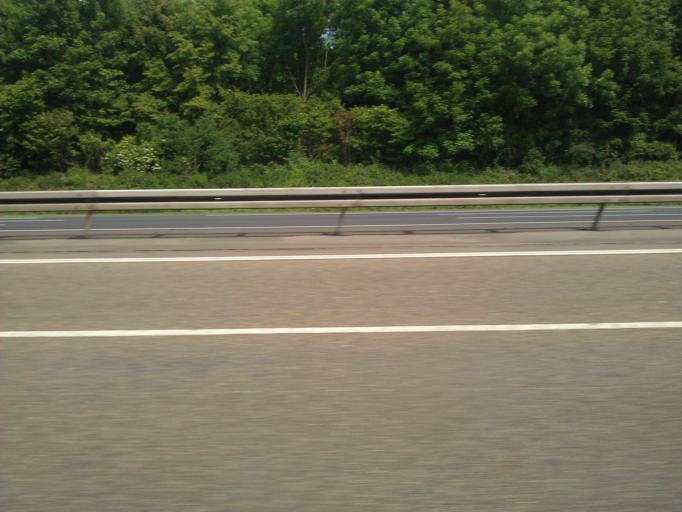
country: DE
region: North Rhine-Westphalia
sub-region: Regierungsbezirk Koln
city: Neustadt/Sued
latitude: 50.8977
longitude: 6.9108
